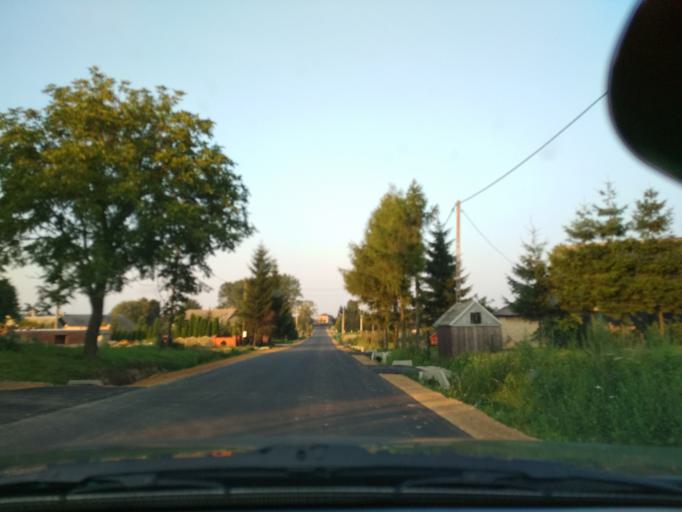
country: PL
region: Lesser Poland Voivodeship
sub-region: Powiat olkuski
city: Wolbrom
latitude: 50.4079
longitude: 19.8255
